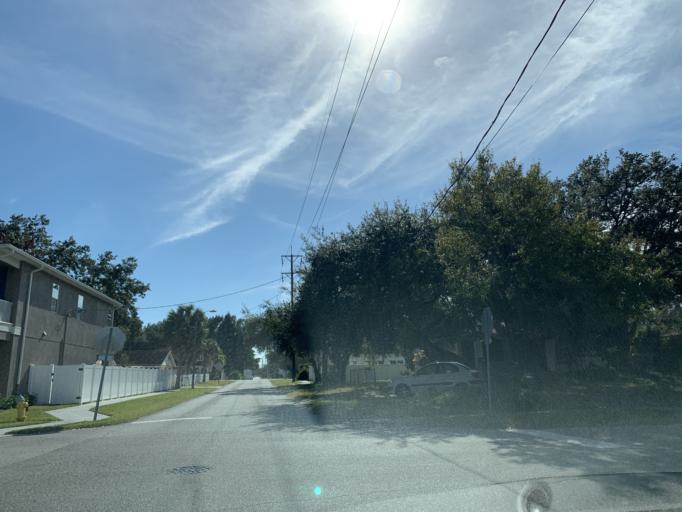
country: US
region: Florida
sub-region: Hillsborough County
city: Tampa
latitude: 27.8900
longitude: -82.4980
